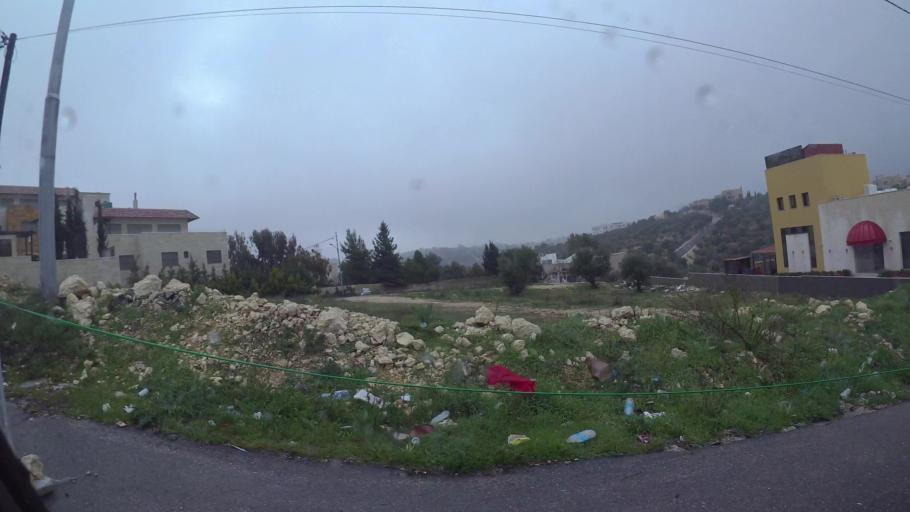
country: JO
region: Amman
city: Wadi as Sir
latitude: 32.0028
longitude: 35.7977
